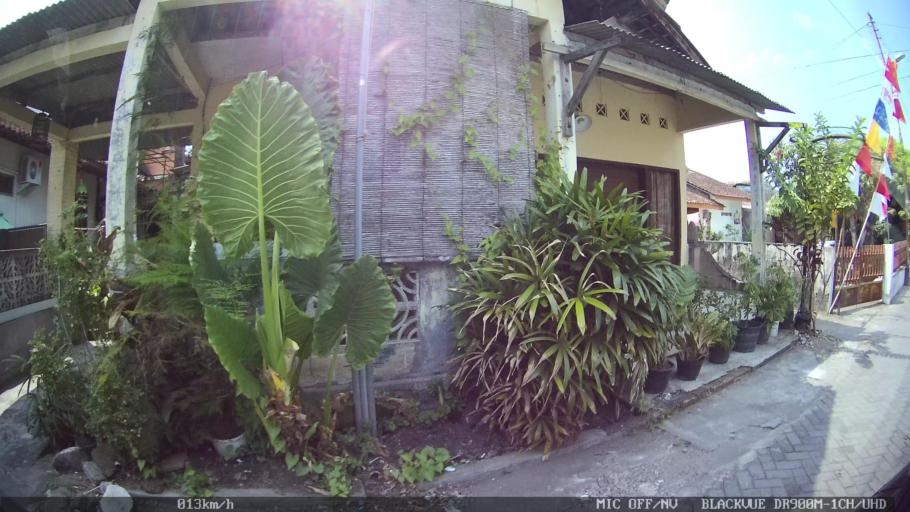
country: ID
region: Daerah Istimewa Yogyakarta
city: Yogyakarta
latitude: -7.8034
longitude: 110.3845
